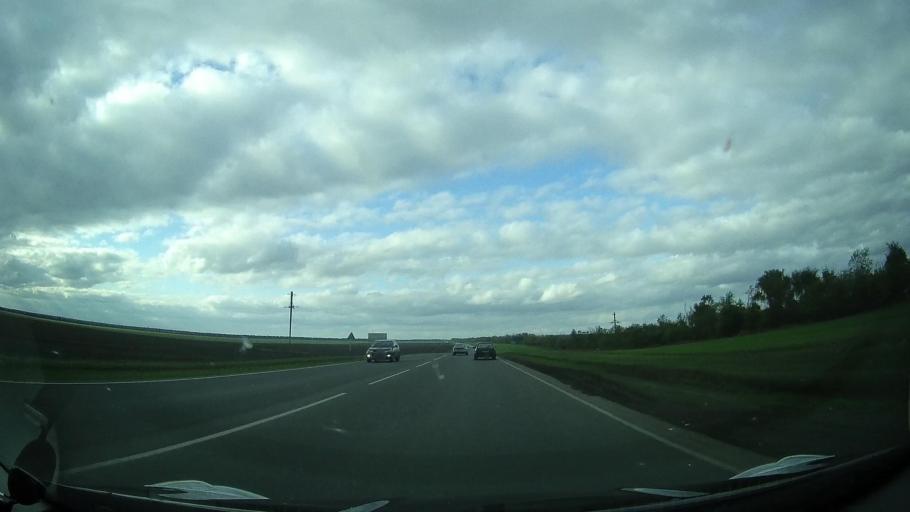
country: RU
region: Rostov
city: Kagal'nitskaya
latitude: 46.8939
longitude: 40.1287
